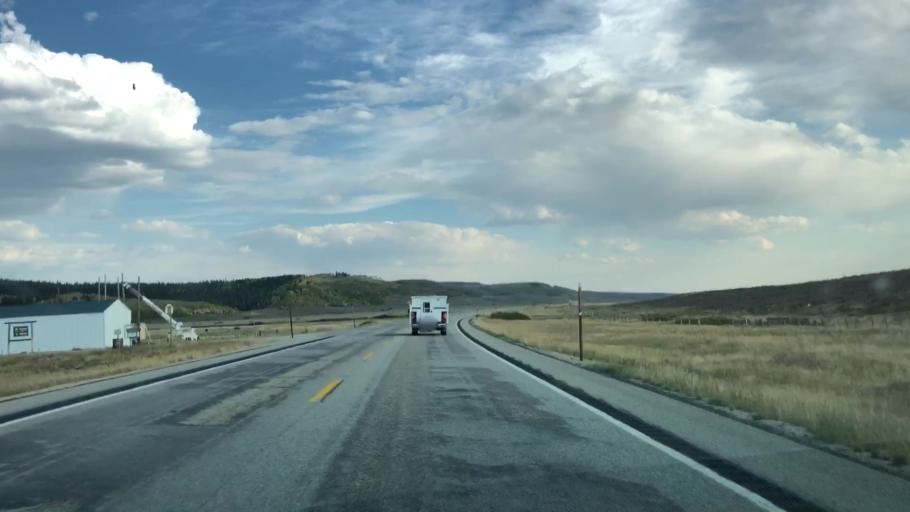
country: US
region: Wyoming
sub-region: Sublette County
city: Pinedale
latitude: 43.1157
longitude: -110.1767
